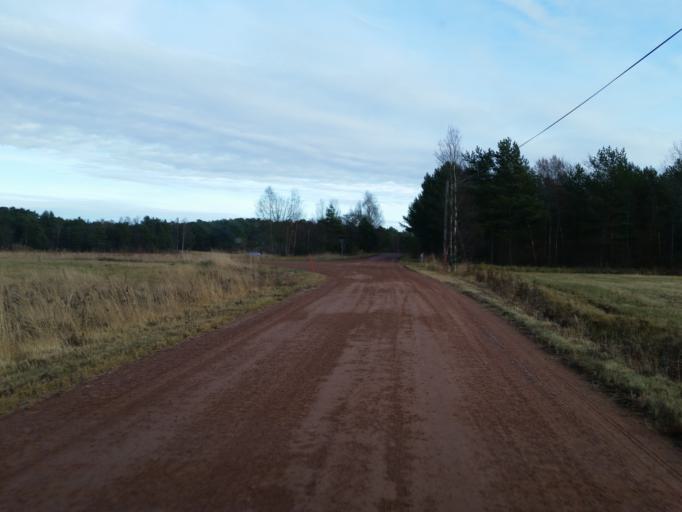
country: AX
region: Alands skaergard
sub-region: Kumlinge
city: Kumlinge
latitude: 60.2540
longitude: 20.8141
